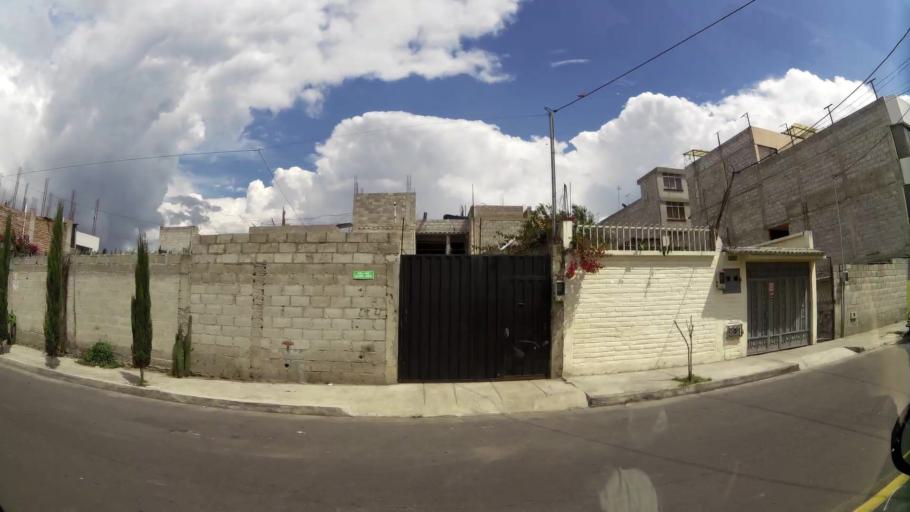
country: EC
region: Pichincha
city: Quito
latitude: -0.0919
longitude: -78.4551
